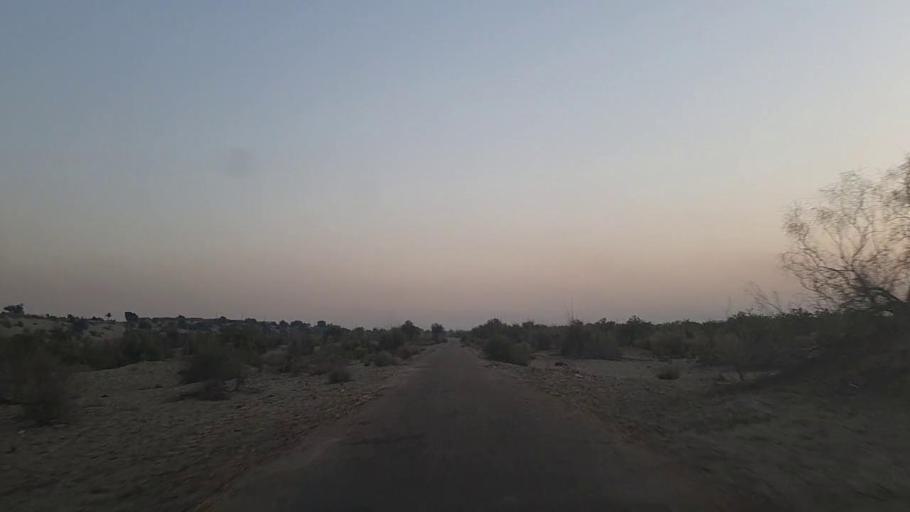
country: PK
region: Sindh
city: Jam Sahib
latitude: 26.3953
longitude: 68.8095
